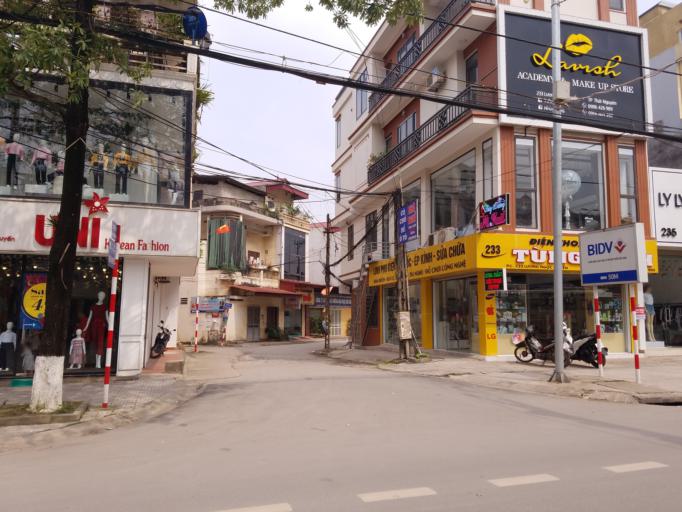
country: VN
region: Thai Nguyen
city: Thanh Pho Thai Nguyen
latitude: 21.5956
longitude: 105.8246
